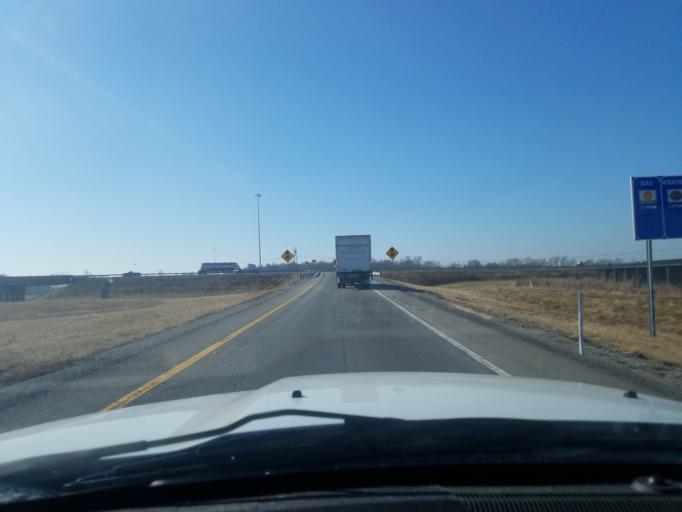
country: US
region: Kentucky
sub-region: Hardin County
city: Elizabethtown
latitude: 37.6560
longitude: -85.8888
